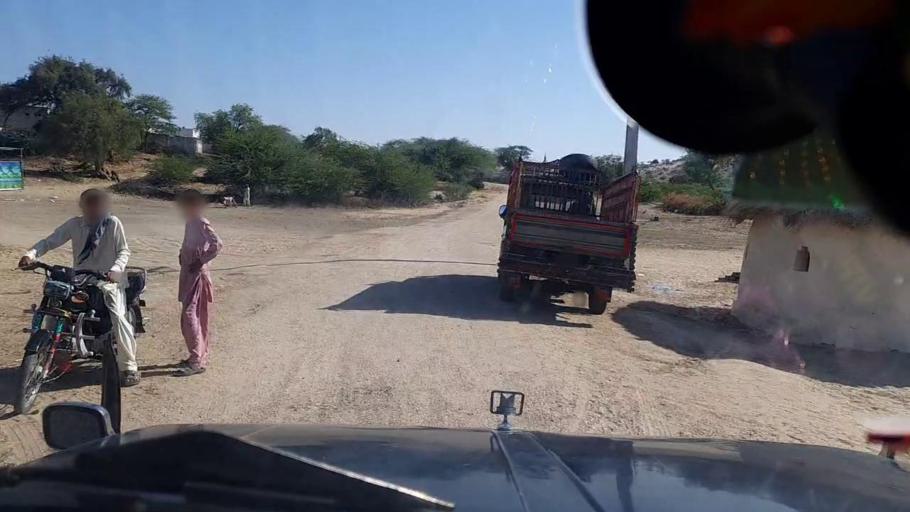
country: PK
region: Sindh
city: Diplo
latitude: 24.4516
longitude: 69.6969
